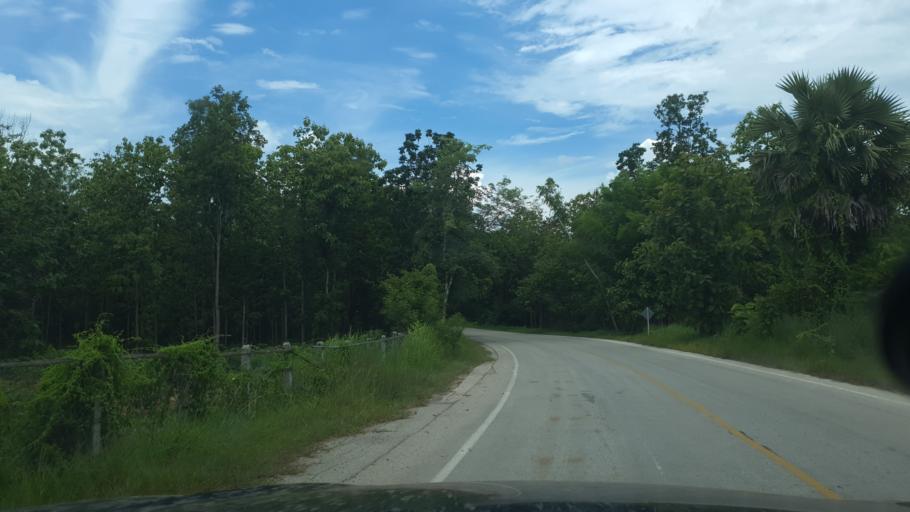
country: TH
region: Lampang
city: Sop Prap
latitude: 17.9179
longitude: 99.3878
